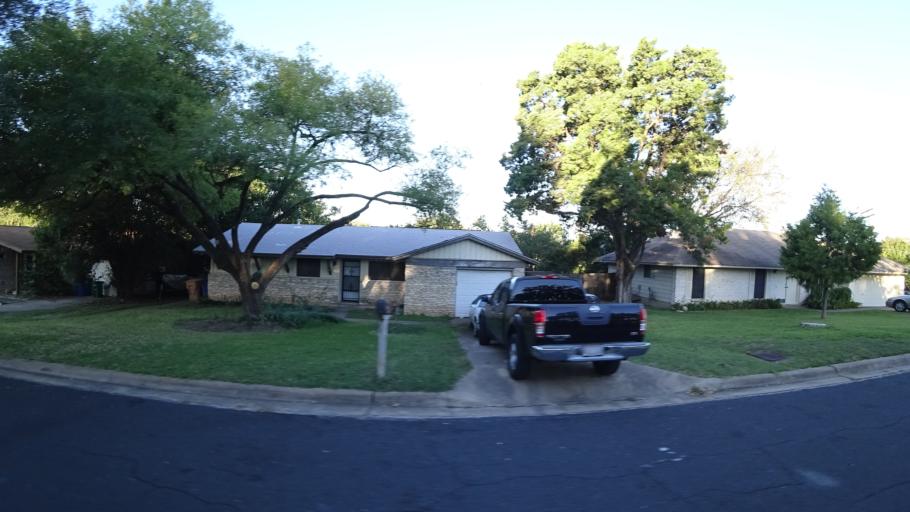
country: US
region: Texas
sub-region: Travis County
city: Austin
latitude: 30.2974
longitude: -97.6787
